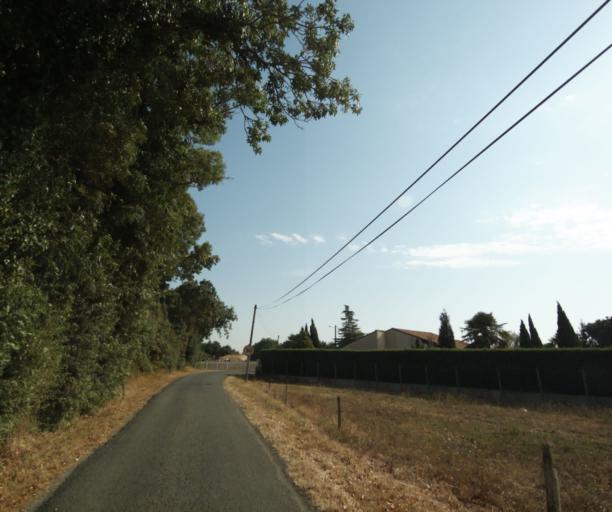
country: FR
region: Poitou-Charentes
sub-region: Departement de la Charente-Maritime
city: Tonnay-Charente
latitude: 45.9659
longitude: -0.8755
